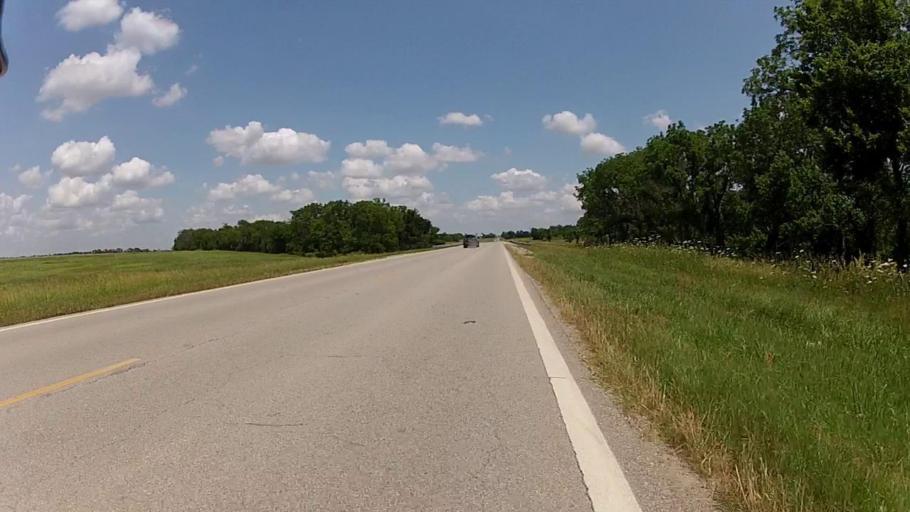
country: US
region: Kansas
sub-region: Labette County
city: Altamont
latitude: 37.1927
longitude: -95.3802
